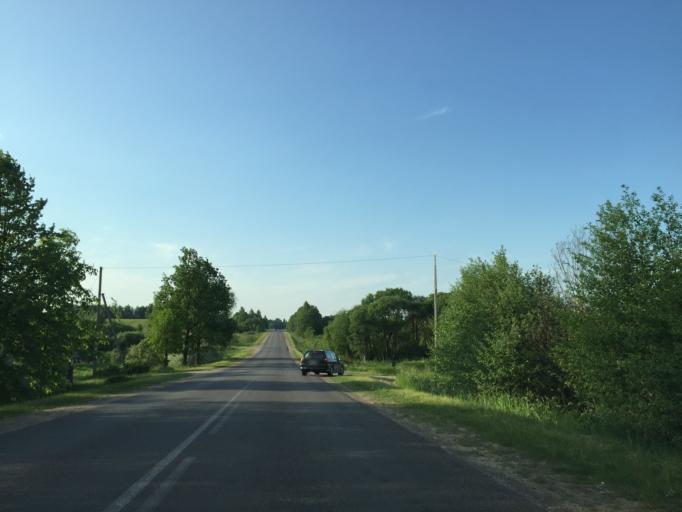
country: LT
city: Plateliai
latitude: 56.0514
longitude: 21.8191
